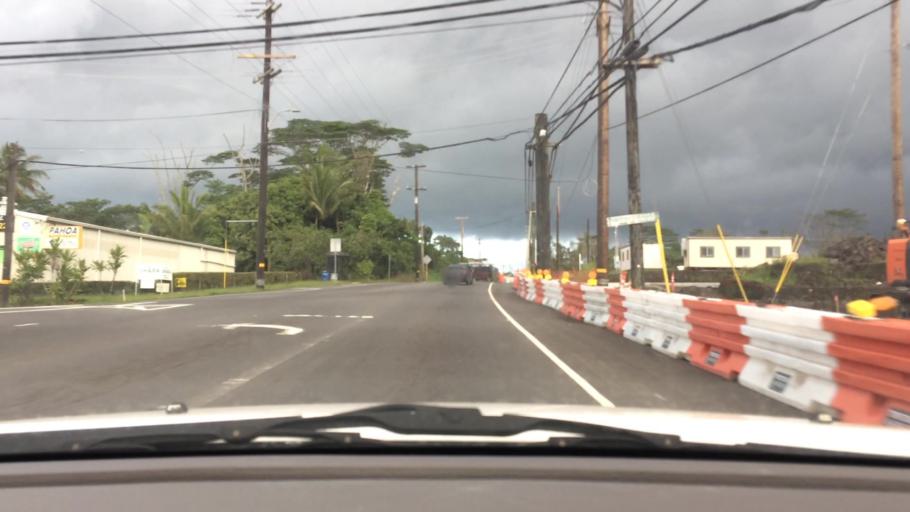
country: US
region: Hawaii
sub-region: Hawaii County
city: Hawaiian Paradise Park
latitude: 19.5039
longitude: -154.9558
